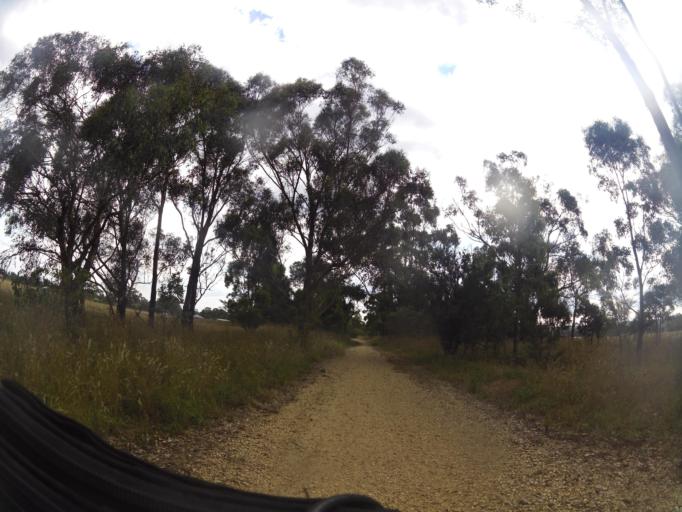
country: AU
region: Victoria
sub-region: Wellington
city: Heyfield
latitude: -38.0505
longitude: 146.6307
